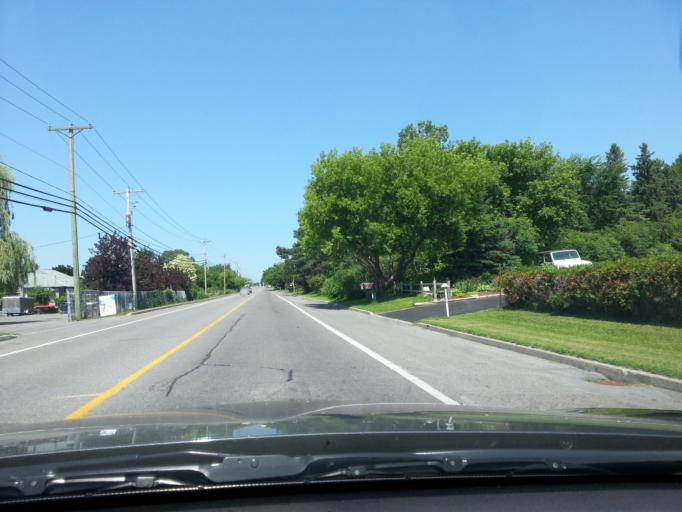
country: CA
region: Ontario
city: Bells Corners
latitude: 45.4049
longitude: -75.8605
